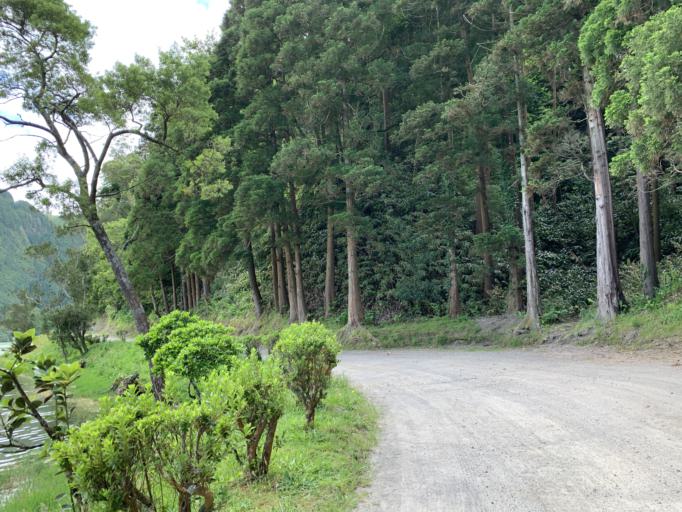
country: PT
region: Azores
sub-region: Ponta Delgada
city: Arrifes
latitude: 37.8515
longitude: -25.7910
